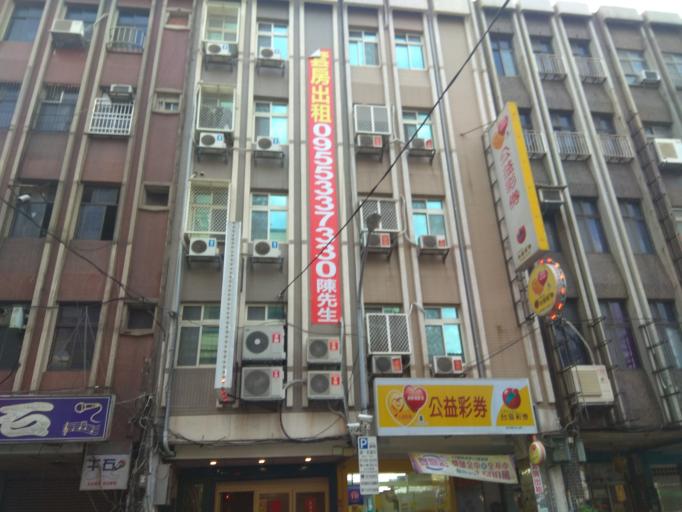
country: TW
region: Taiwan
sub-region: Taoyuan
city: Taoyuan
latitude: 24.9915
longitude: 121.3080
